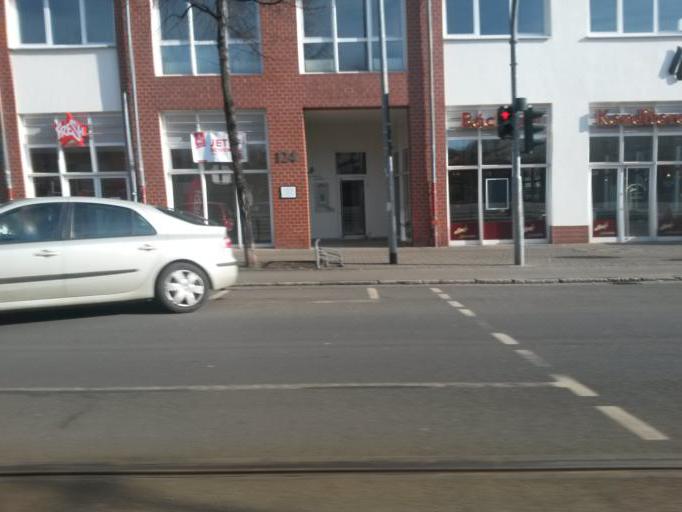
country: DE
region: Thuringia
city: Erfurt
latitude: 50.9968
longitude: 11.0265
